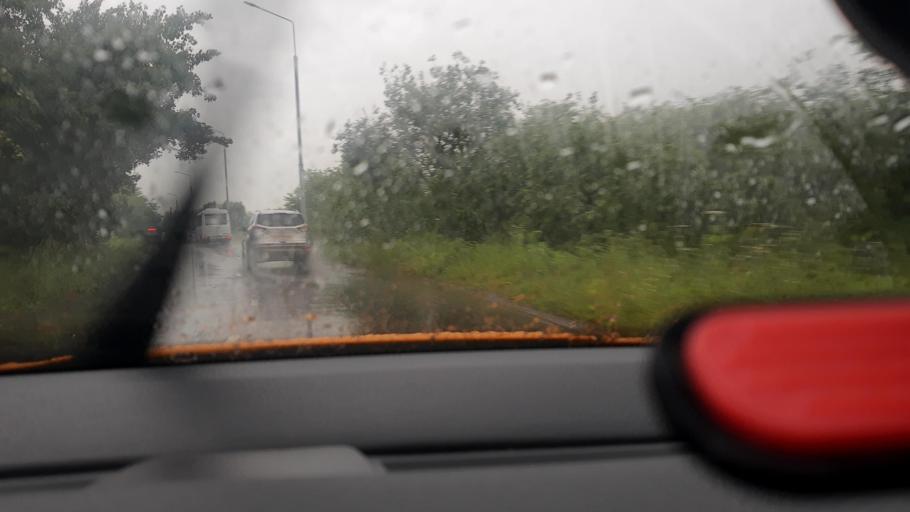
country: RU
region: Moskovskaya
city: Novopodrezkovo
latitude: 55.9333
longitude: 37.3816
